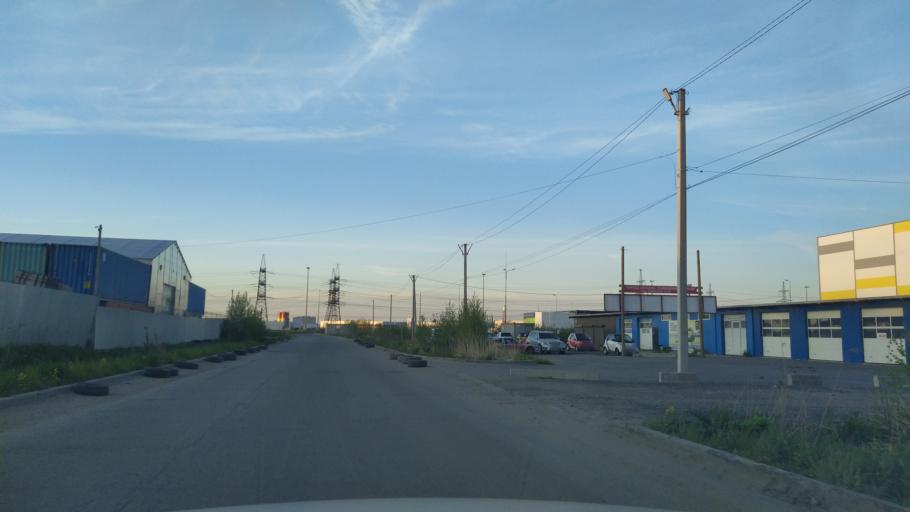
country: RU
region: St.-Petersburg
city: Obukhovo
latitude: 59.8080
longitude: 30.4629
